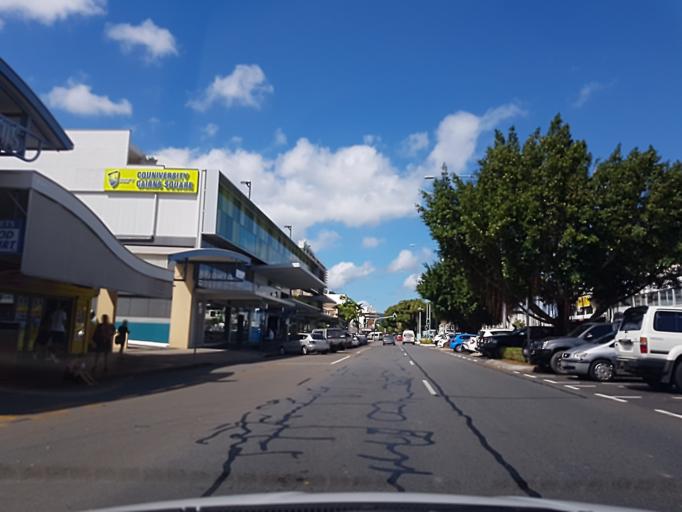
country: AU
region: Queensland
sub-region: Cairns
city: Cairns
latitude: -16.9204
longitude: 145.7761
